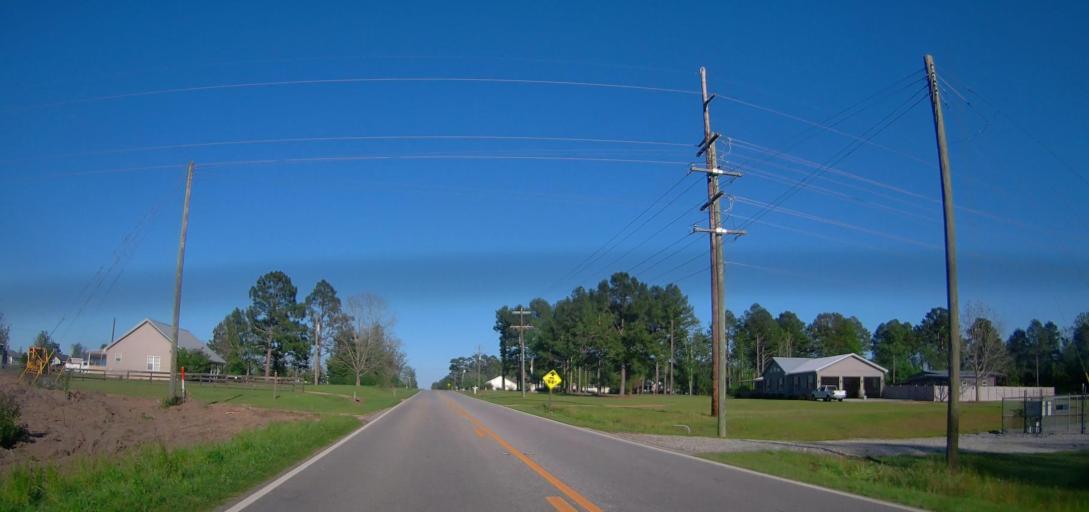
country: US
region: Georgia
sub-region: Ben Hill County
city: Fitzgerald
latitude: 31.7432
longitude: -83.2383
